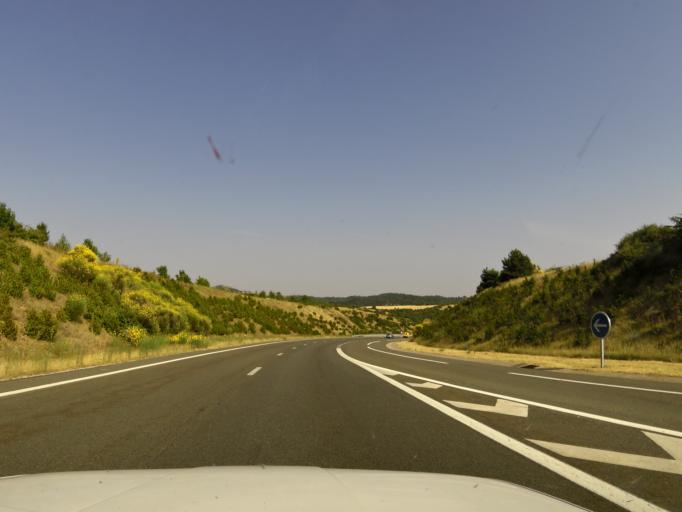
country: FR
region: Languedoc-Roussillon
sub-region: Departement de l'Herault
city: Lodeve
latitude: 43.8464
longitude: 3.3094
